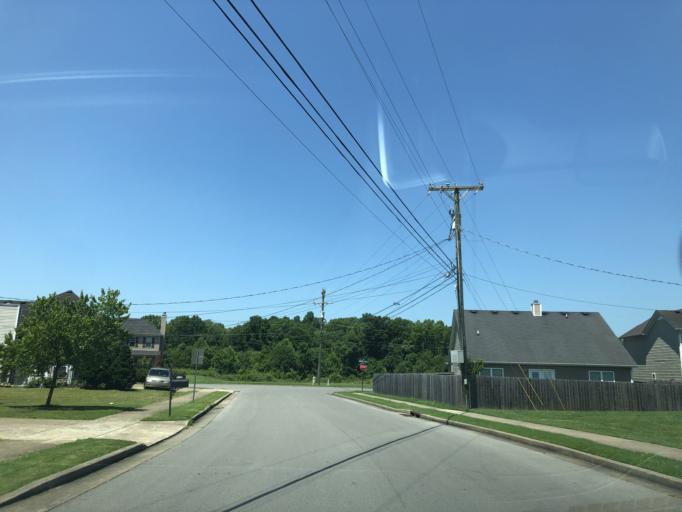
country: US
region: Tennessee
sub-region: Williamson County
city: Nolensville
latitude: 36.0338
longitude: -86.6708
